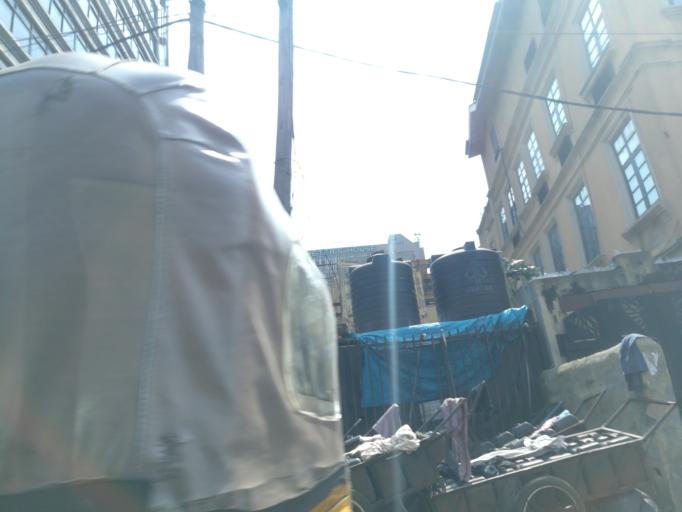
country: NG
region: Lagos
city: Lagos
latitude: 6.4517
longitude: 3.3934
